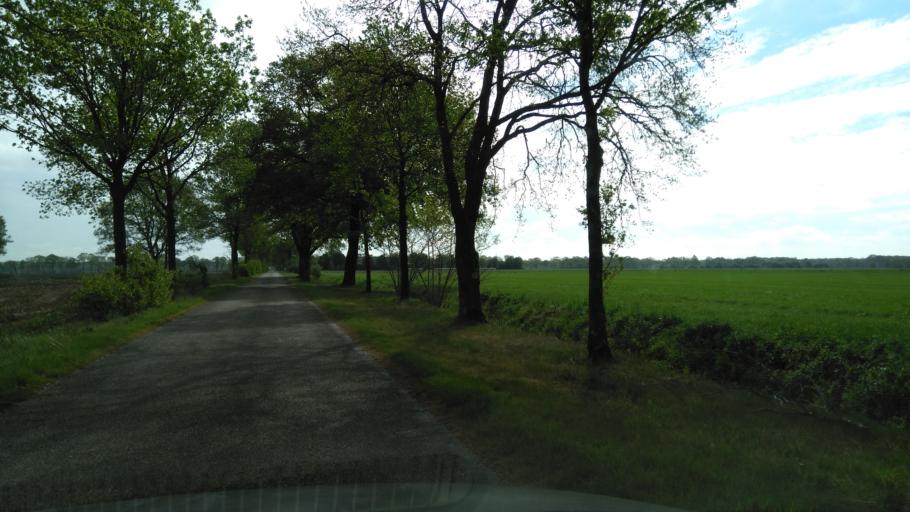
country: BE
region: Flanders
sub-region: Provincie Antwerpen
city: Baarle-Hertog
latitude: 51.4140
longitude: 4.9104
